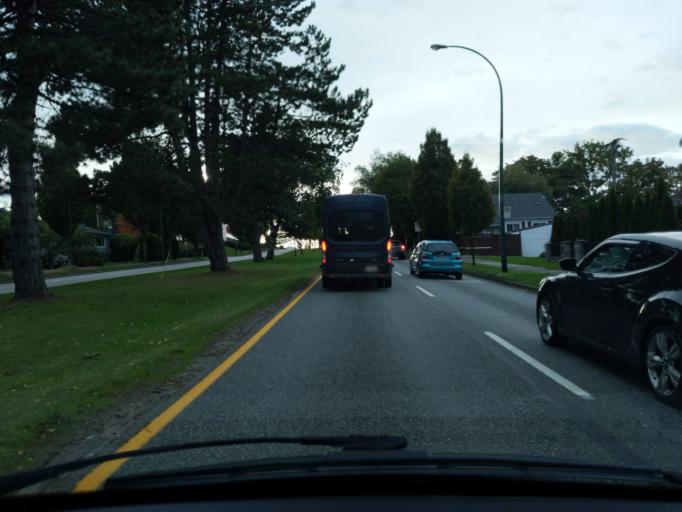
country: CA
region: British Columbia
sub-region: Fraser Valley Regional District
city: North Vancouver
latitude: 49.2696
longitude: -123.0535
